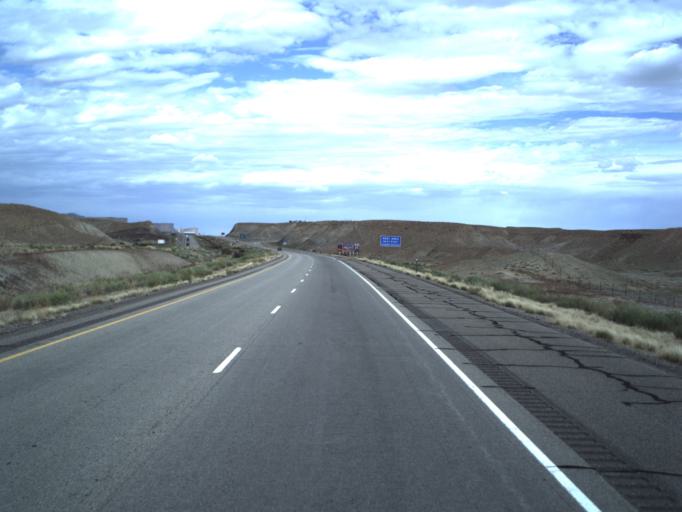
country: US
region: Utah
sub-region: Grand County
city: Moab
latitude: 38.9348
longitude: -109.8451
